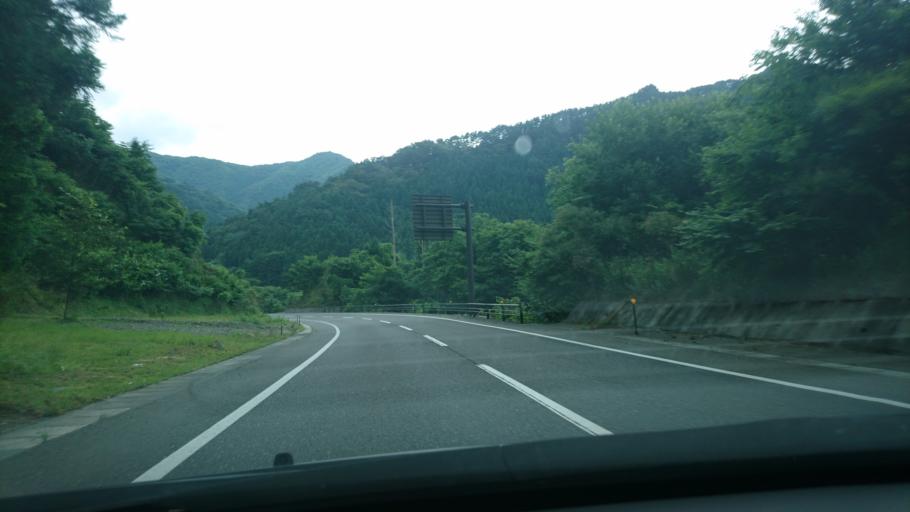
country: JP
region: Iwate
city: Kamaishi
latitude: 39.2997
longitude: 141.8808
